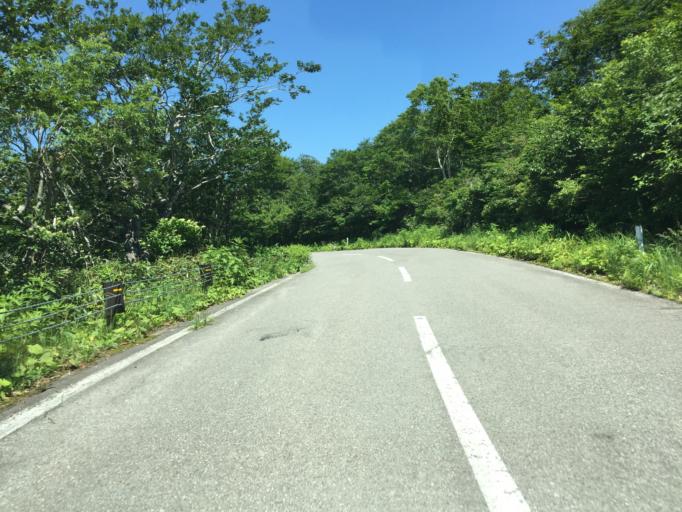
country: JP
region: Fukushima
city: Inawashiro
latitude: 37.6774
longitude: 140.2349
